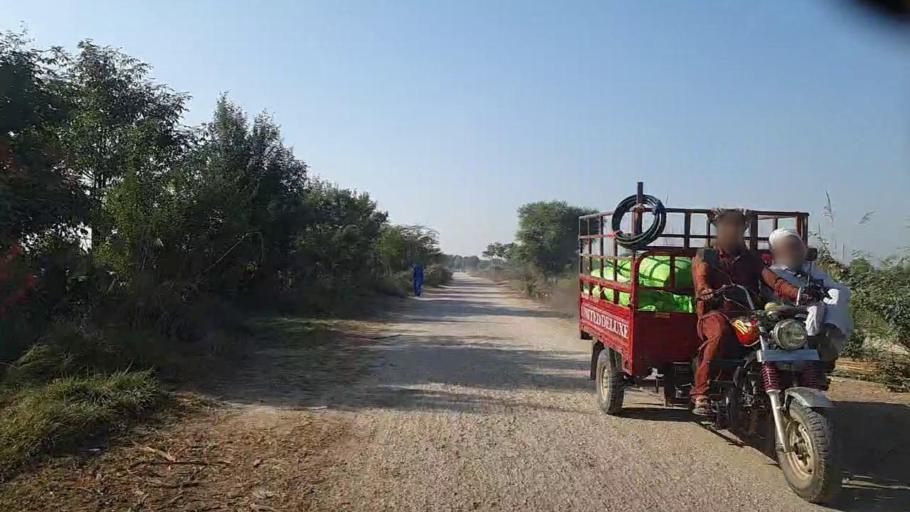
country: PK
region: Sindh
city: Darya Khan Marri
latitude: 26.6770
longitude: 68.3746
